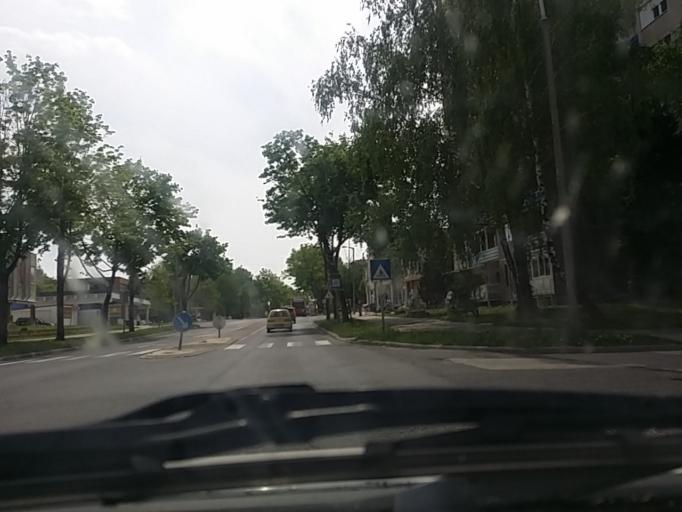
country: HU
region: Zala
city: Nagykanizsa
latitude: 46.4605
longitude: 17.0095
